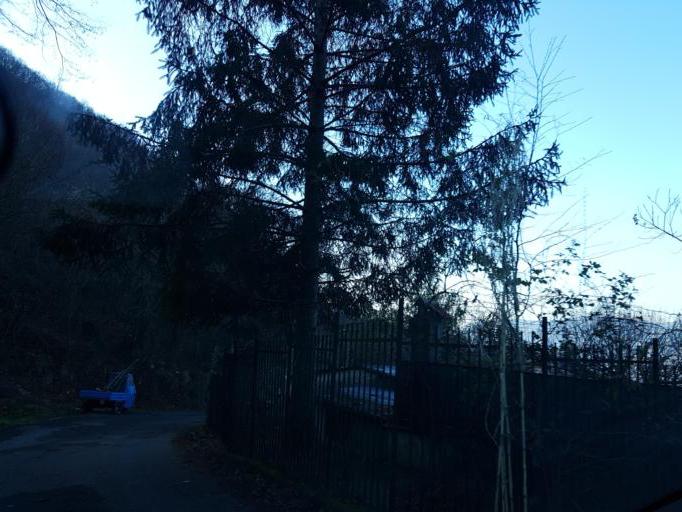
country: IT
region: Liguria
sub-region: Provincia di Genova
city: Manesseno
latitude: 44.4662
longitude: 8.9366
